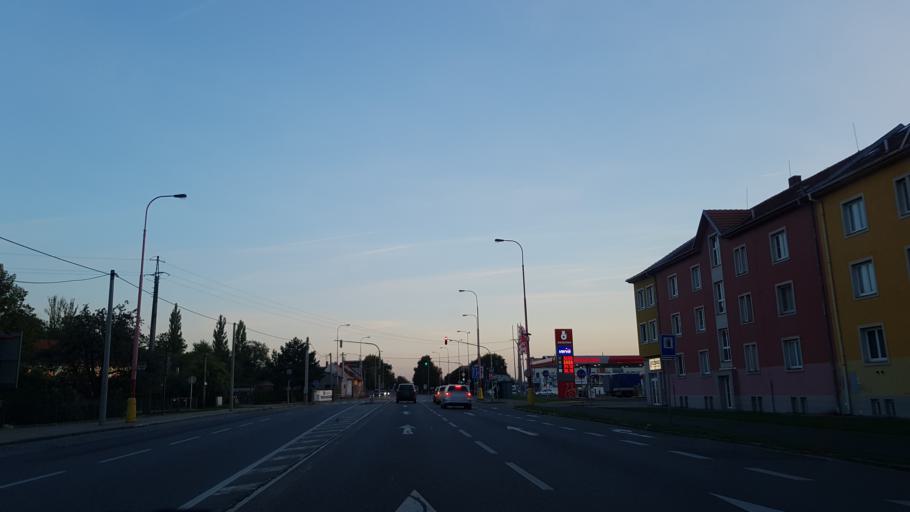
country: CZ
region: Zlin
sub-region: Okres Uherske Hradiste
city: Uherske Hradiste
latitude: 49.0598
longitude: 17.4665
